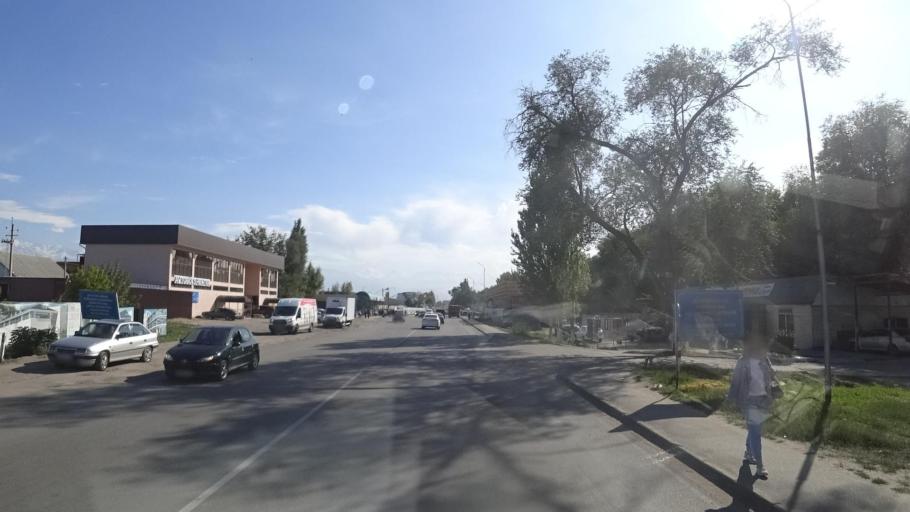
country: KZ
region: Almaty Oblysy
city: Energeticheskiy
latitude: 43.4213
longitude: 77.0230
